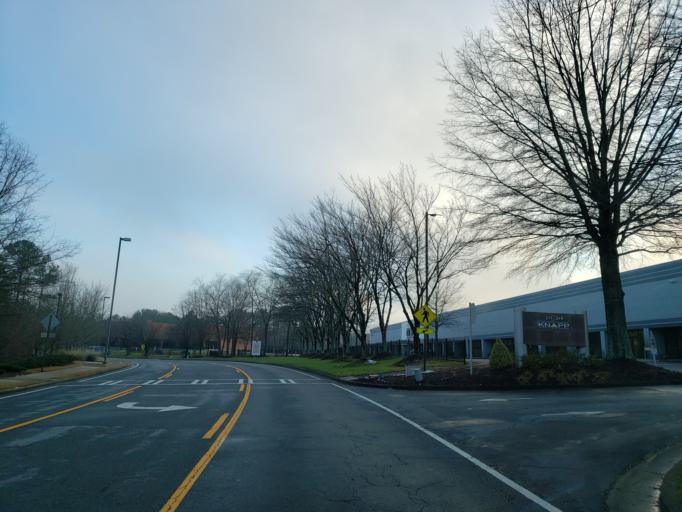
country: US
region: Georgia
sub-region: Cobb County
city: Kennesaw
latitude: 34.0082
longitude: -84.5963
